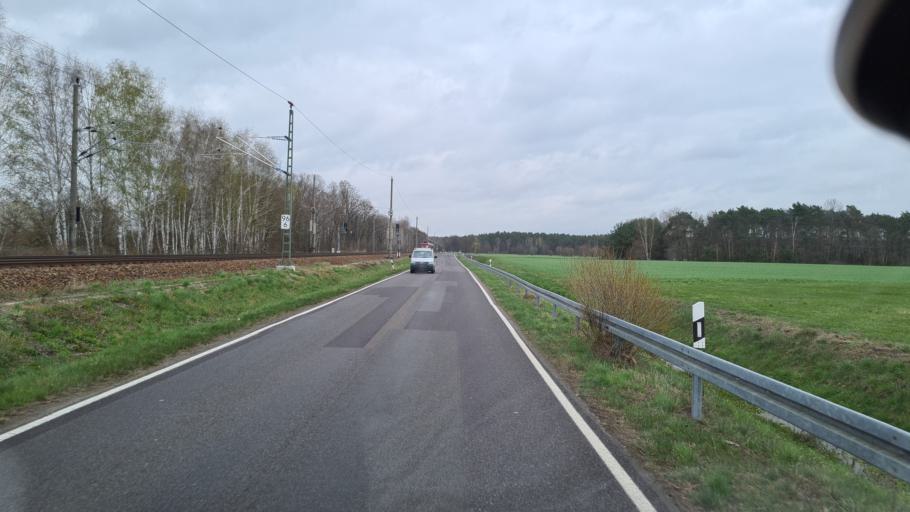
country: DE
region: Brandenburg
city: Ruhland
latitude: 51.4576
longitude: 13.8919
